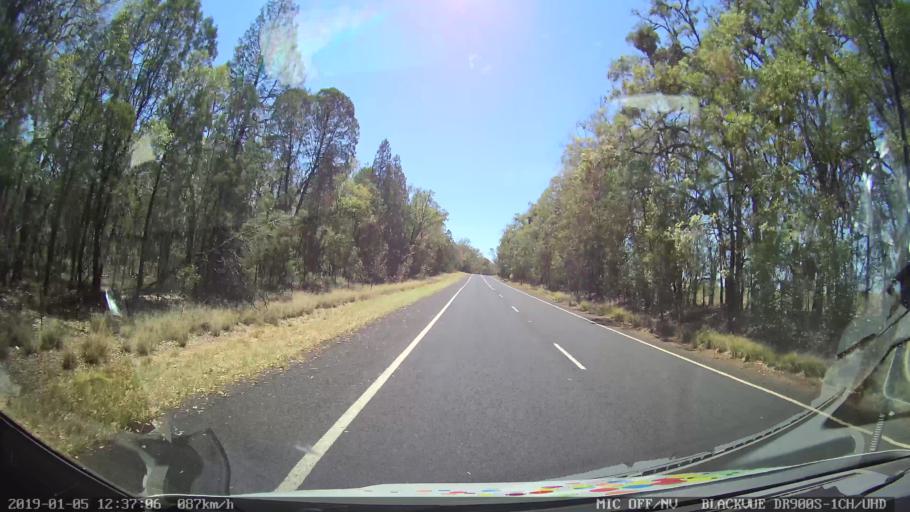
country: AU
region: New South Wales
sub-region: Warrumbungle Shire
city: Coonabarabran
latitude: -31.2049
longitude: 149.4500
